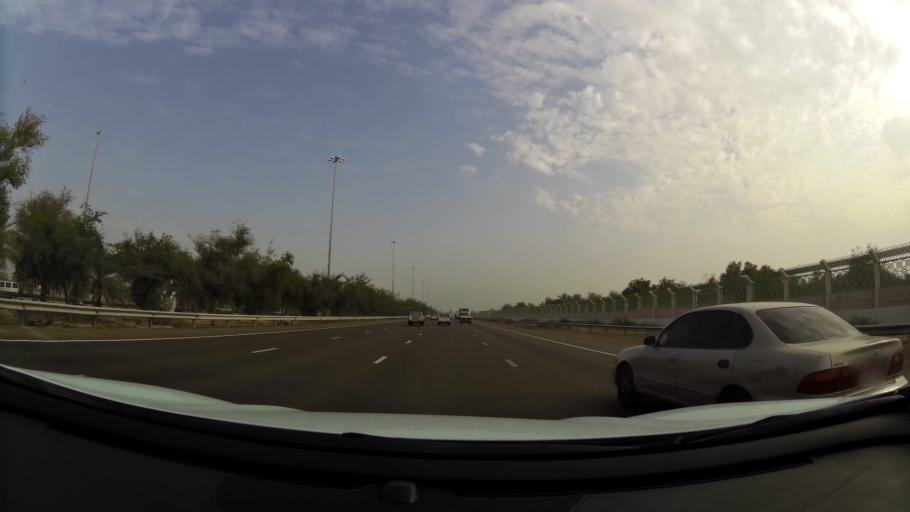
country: AE
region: Abu Dhabi
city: Abu Dhabi
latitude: 24.6044
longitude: 54.7097
